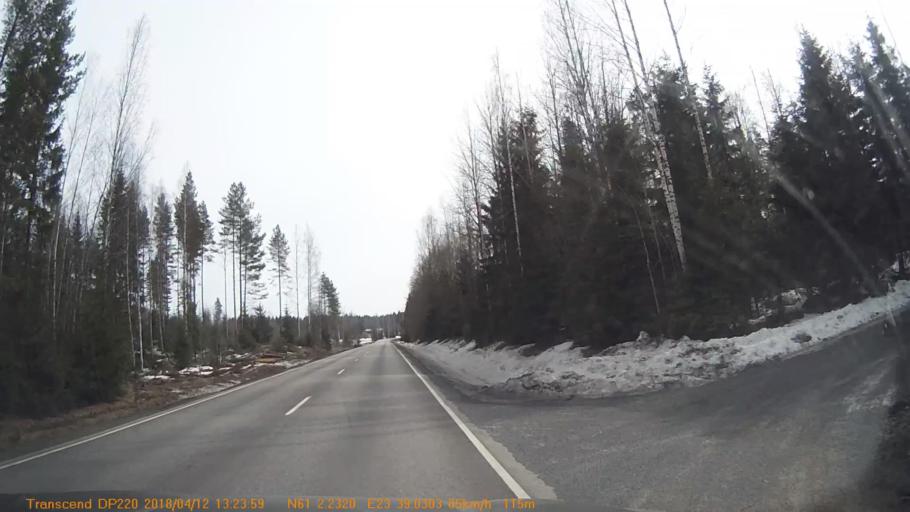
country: FI
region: Pirkanmaa
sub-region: Etelae-Pirkanmaa
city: Kylmaekoski
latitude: 61.0363
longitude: 23.6520
